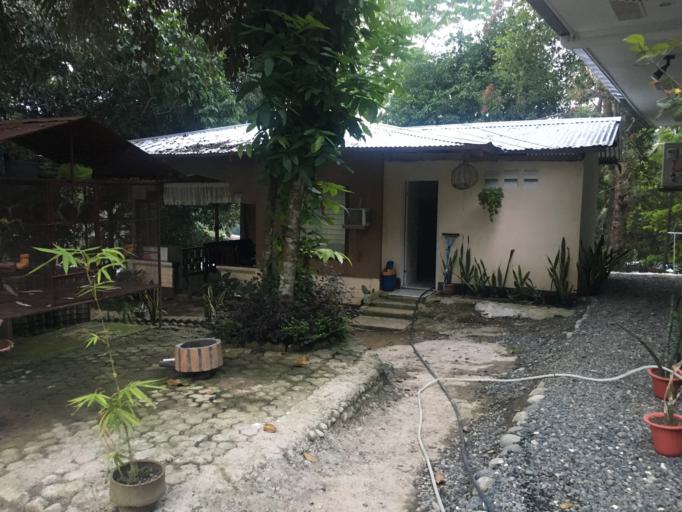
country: PH
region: Davao
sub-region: Province of Davao del Norte
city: Magatos
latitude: 7.6035
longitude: 125.7537
